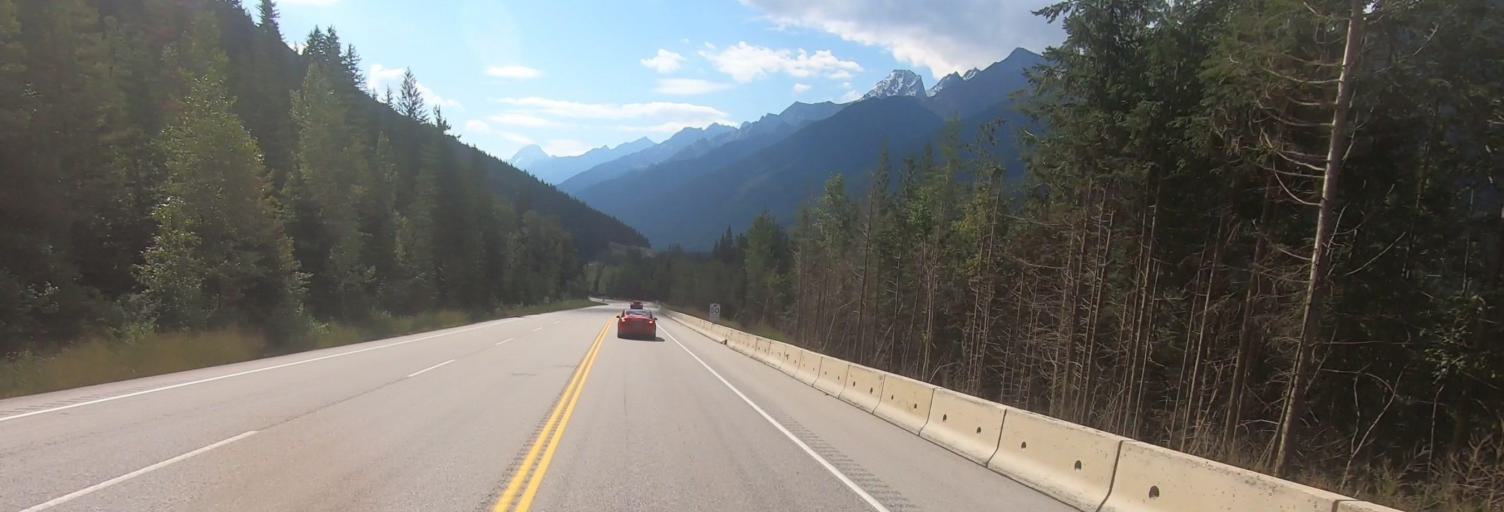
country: CA
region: British Columbia
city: Golden
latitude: 51.4465
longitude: -117.4783
